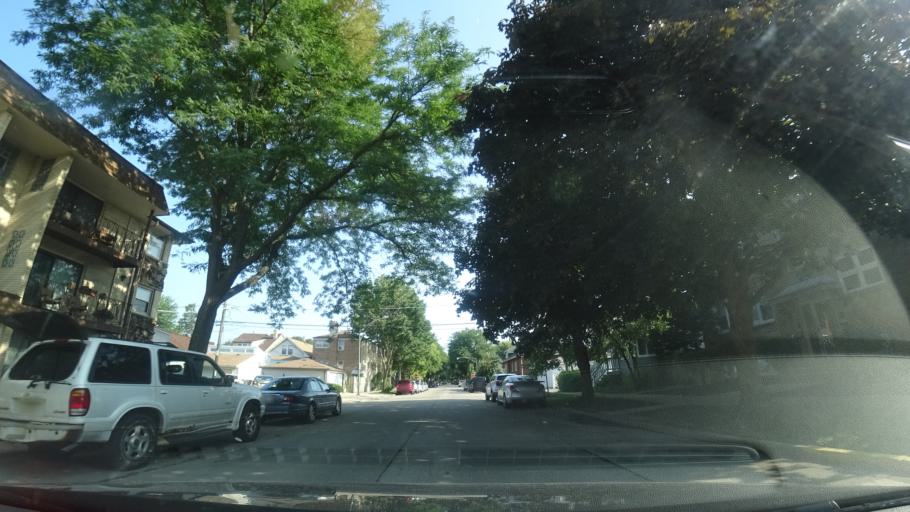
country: US
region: Illinois
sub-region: Cook County
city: Harwood Heights
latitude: 41.9637
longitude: -87.7649
